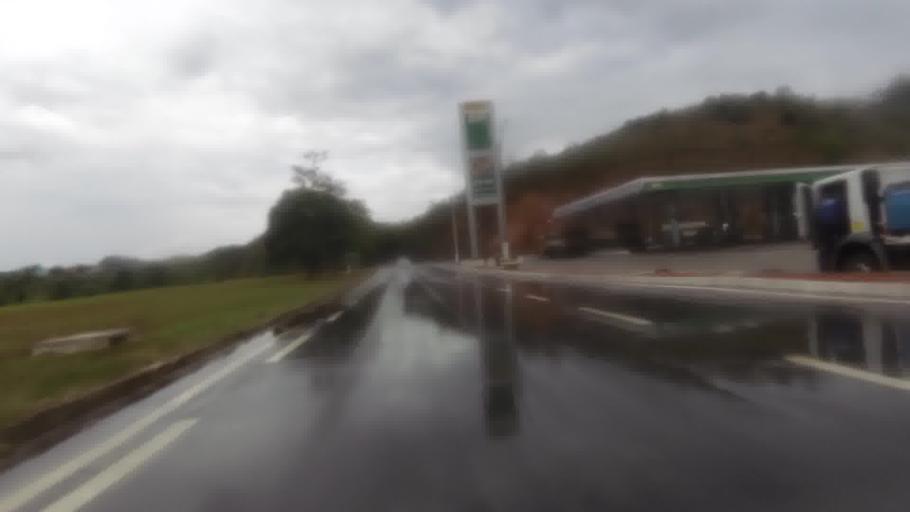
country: BR
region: Espirito Santo
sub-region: Cachoeiro De Itapemirim
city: Cachoeiro de Itapemirim
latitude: -21.0100
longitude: -41.1443
